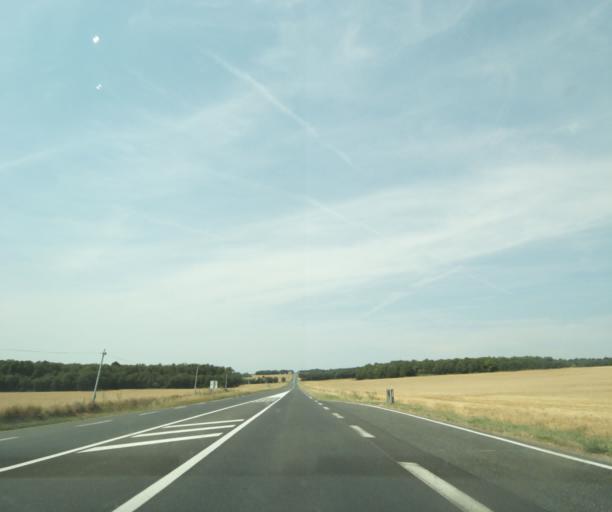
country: FR
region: Centre
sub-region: Departement d'Indre-et-Loire
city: Sainte-Maure-de-Touraine
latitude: 47.0768
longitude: 0.6131
